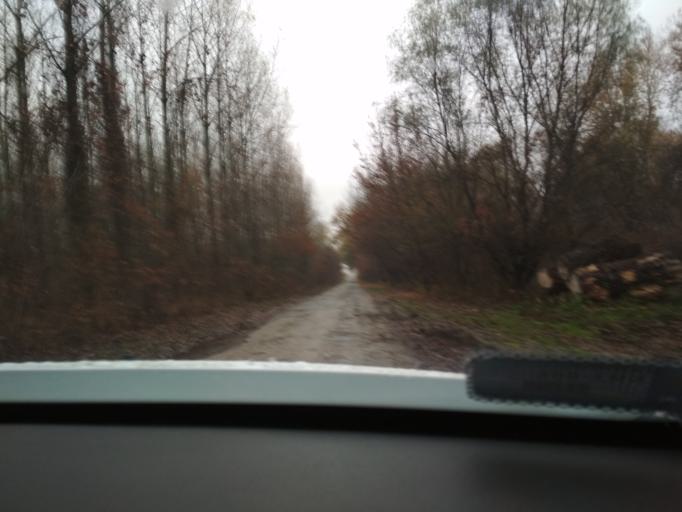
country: HU
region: Csongrad
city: Mindszent
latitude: 46.5344
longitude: 20.1597
